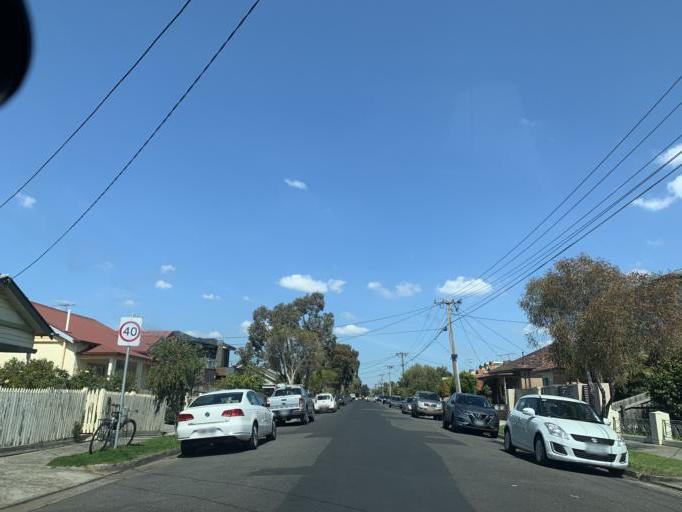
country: AU
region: Victoria
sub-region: Moreland
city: Coburg North
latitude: -37.7339
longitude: 144.9602
